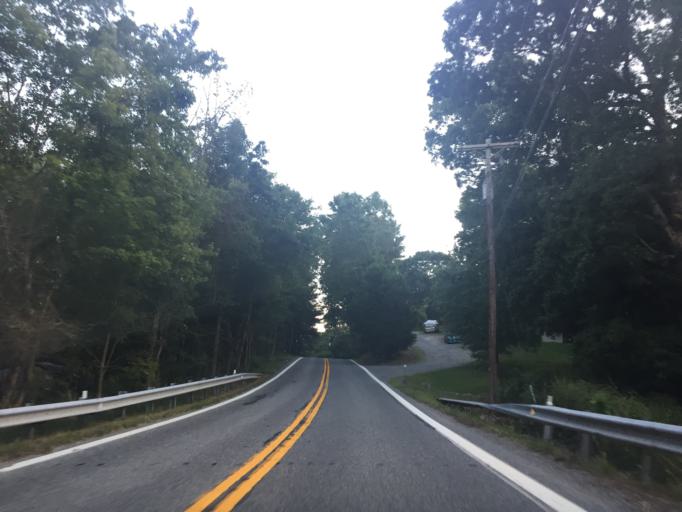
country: US
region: Pennsylvania
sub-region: York County
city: Susquehanna Trails
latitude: 39.6719
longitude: -76.3177
